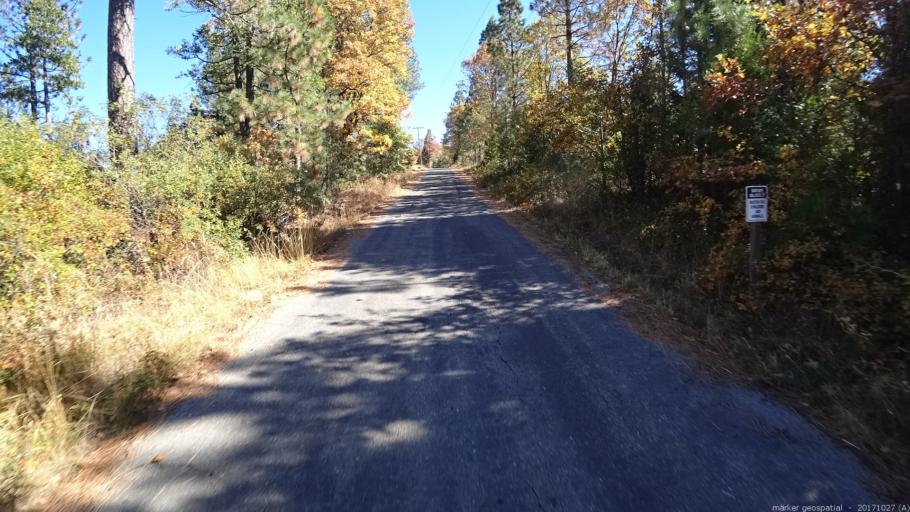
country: US
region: California
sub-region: Shasta County
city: Shingletown
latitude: 40.7209
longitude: -121.9265
